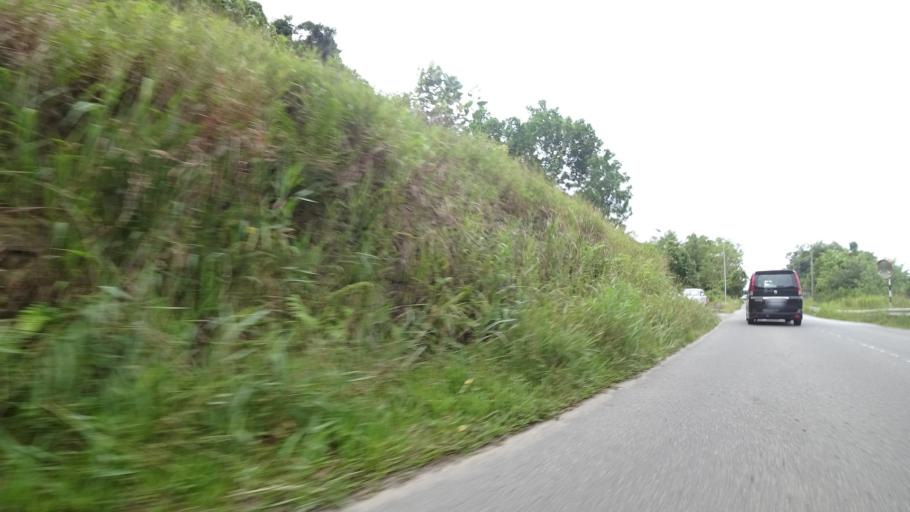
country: BN
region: Brunei and Muara
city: Bandar Seri Begawan
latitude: 4.8593
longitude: 114.9522
